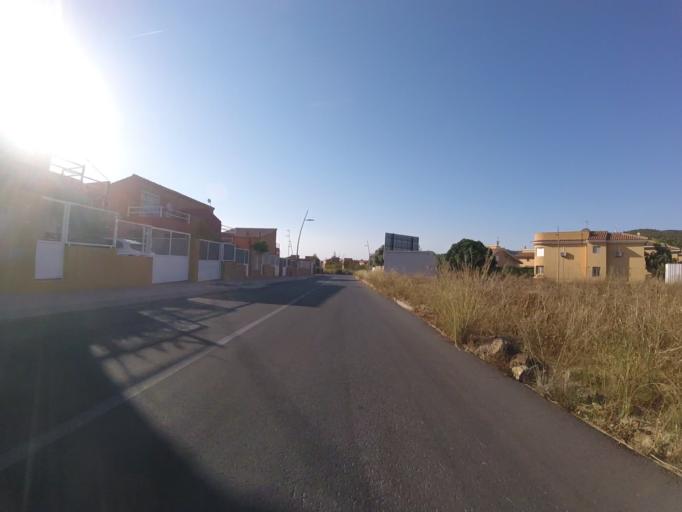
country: ES
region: Valencia
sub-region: Provincia de Castello
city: Peniscola
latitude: 40.3875
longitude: 0.3772
